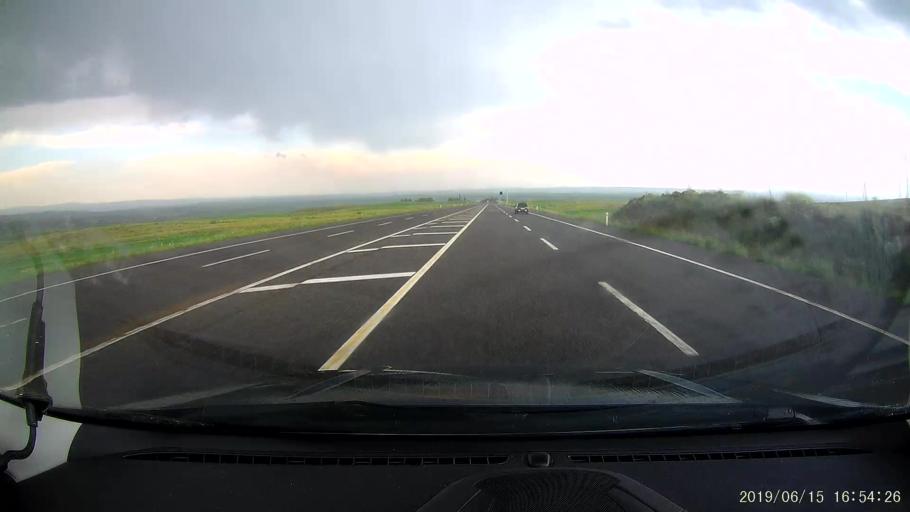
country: TR
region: Kars
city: Susuz
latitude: 40.7905
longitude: 43.1241
